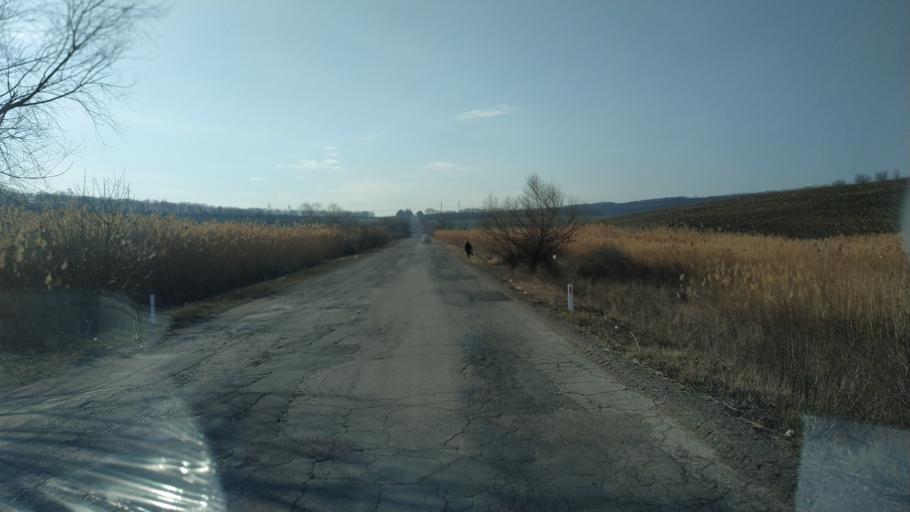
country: MD
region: Chisinau
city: Singera
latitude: 46.8829
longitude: 29.0393
